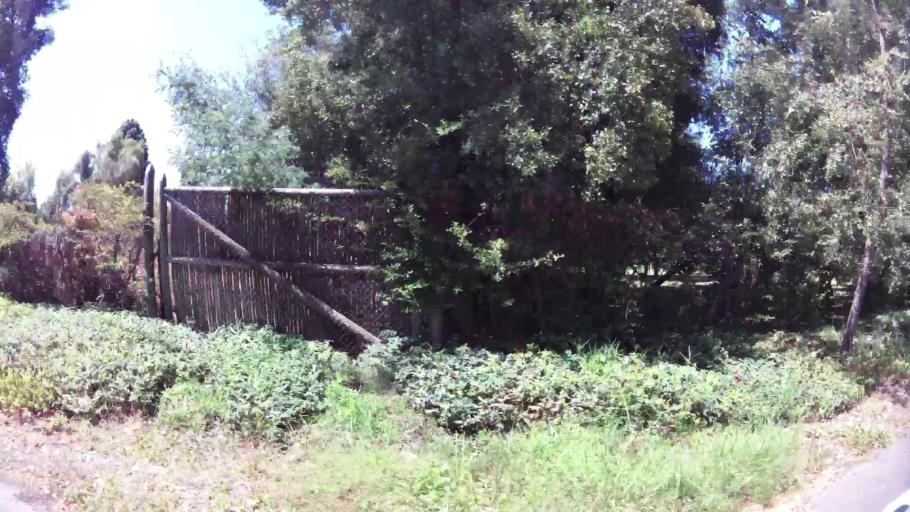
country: CL
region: Maule
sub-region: Provincia de Curico
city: Curico
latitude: -34.9957
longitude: -71.2112
